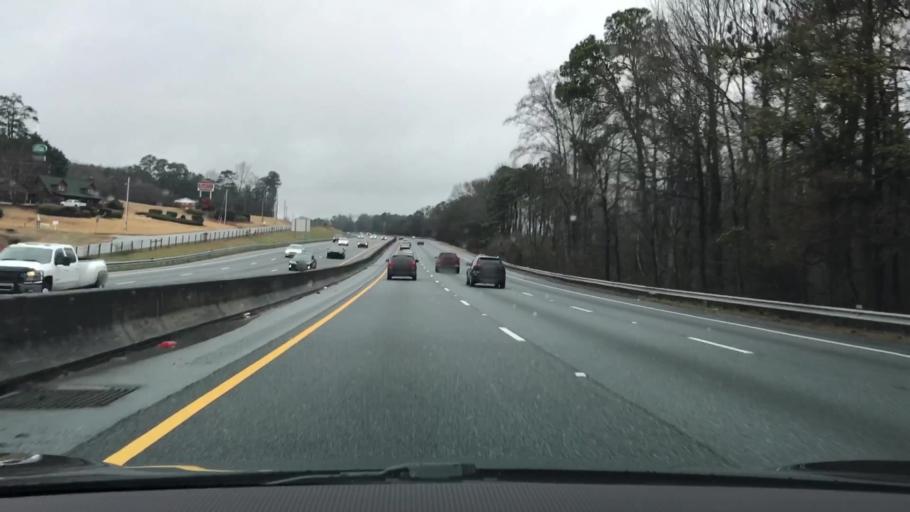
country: US
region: Georgia
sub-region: Newton County
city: Porterdale
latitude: 33.6250
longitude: -83.9395
